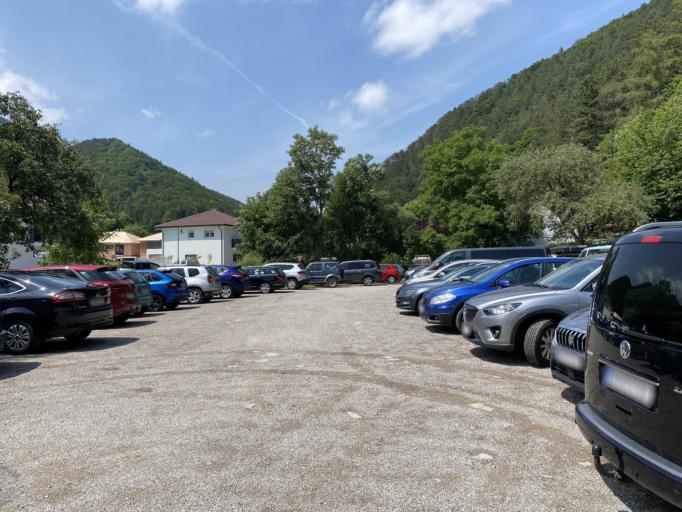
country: AT
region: Lower Austria
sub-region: Politischer Bezirk Baden
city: Furth an der Triesting
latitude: 47.9733
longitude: 15.9730
